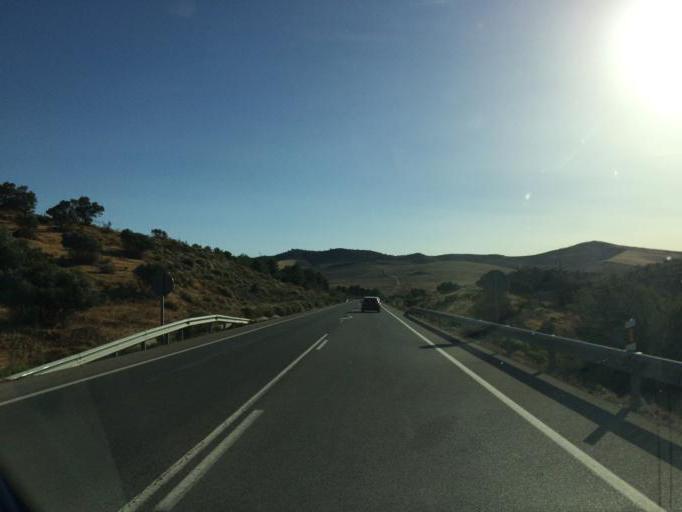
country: ES
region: Andalusia
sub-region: Provincia de Malaga
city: Campillos
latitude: 36.9715
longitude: -4.8389
